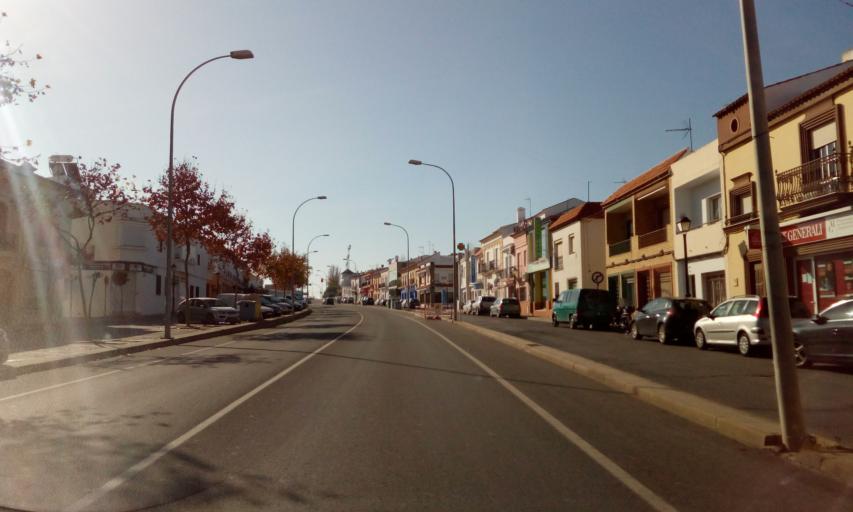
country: ES
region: Andalusia
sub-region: Provincia de Huelva
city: Lepe
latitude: 37.2487
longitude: -7.2030
